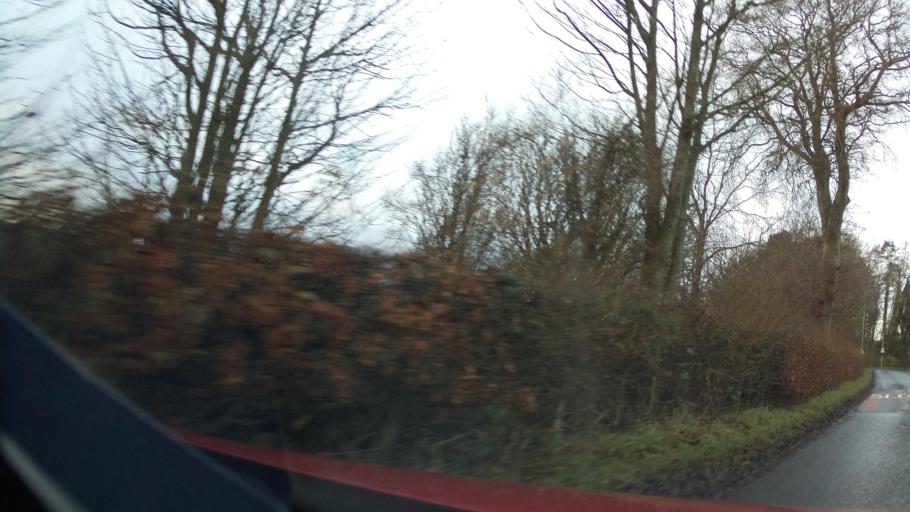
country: GB
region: Scotland
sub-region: Angus
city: Letham
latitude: 56.5320
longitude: -2.7972
